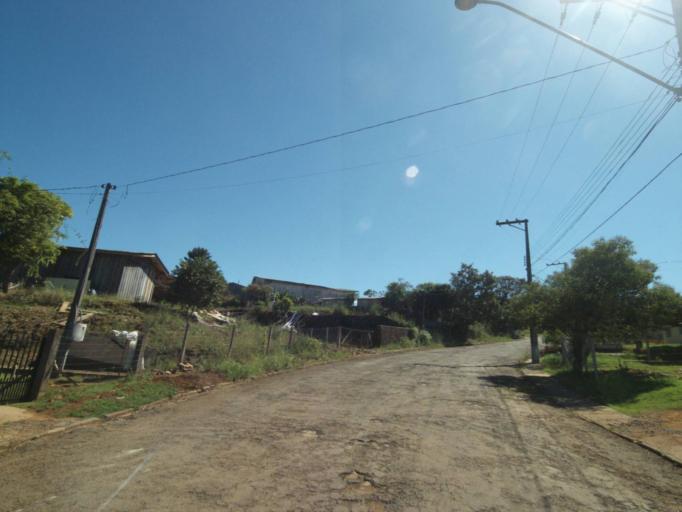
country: BR
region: Parana
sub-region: Pinhao
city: Pinhao
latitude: -25.8360
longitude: -52.0251
